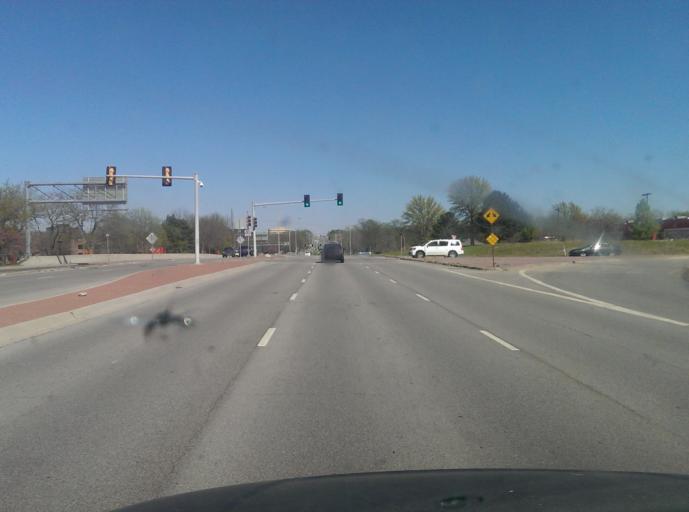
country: US
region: Kansas
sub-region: Johnson County
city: Lenexa
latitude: 38.9274
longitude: -94.7041
